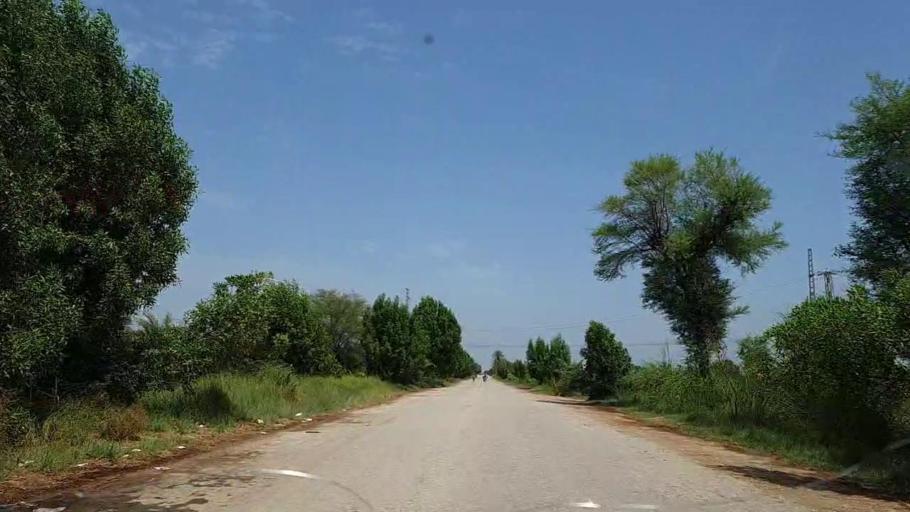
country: PK
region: Sindh
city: Naushahro Firoz
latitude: 26.8322
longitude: 68.1352
